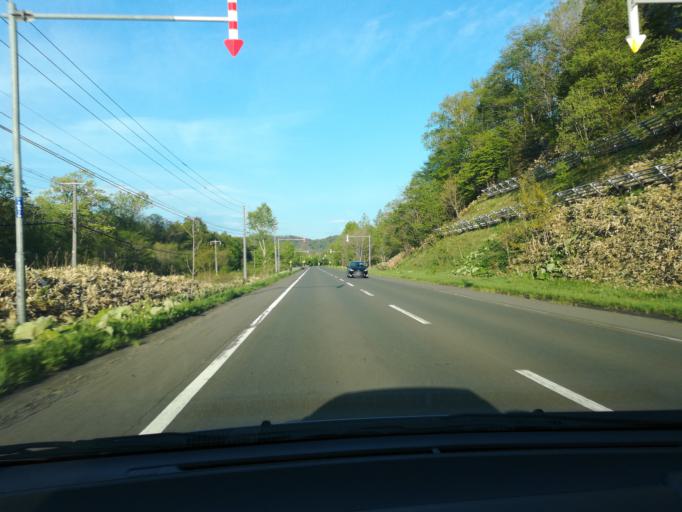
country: JP
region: Hokkaido
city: Shimo-furano
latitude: 43.1357
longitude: 142.6402
